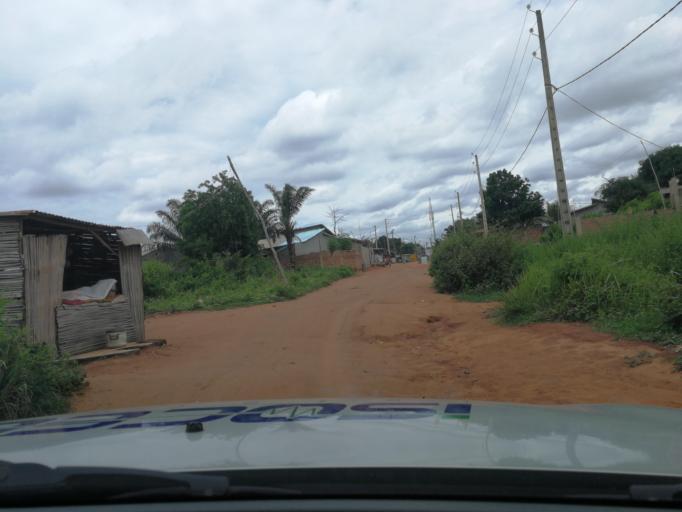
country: BJ
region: Atlantique
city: Abomey-Calavi
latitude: 6.4350
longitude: 2.3062
